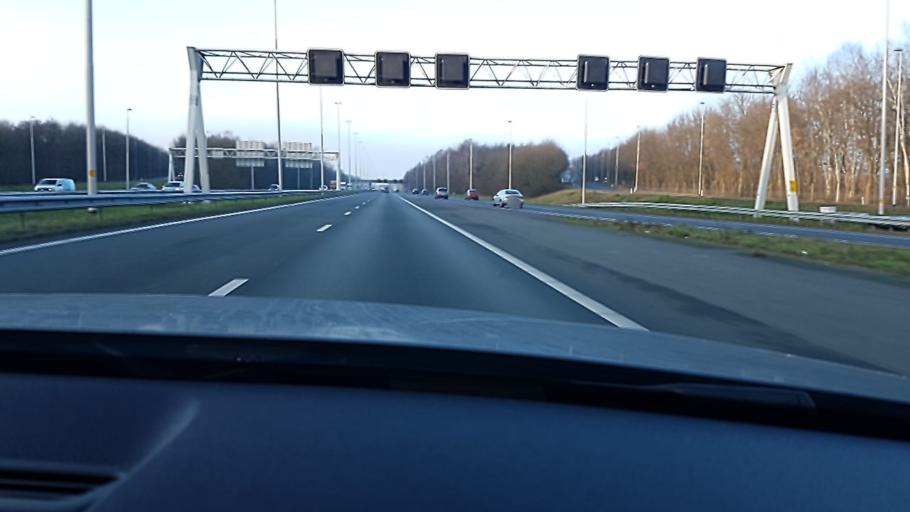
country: NL
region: Overijssel
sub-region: Gemeente Borne
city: Borne
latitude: 52.2900
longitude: 6.7339
